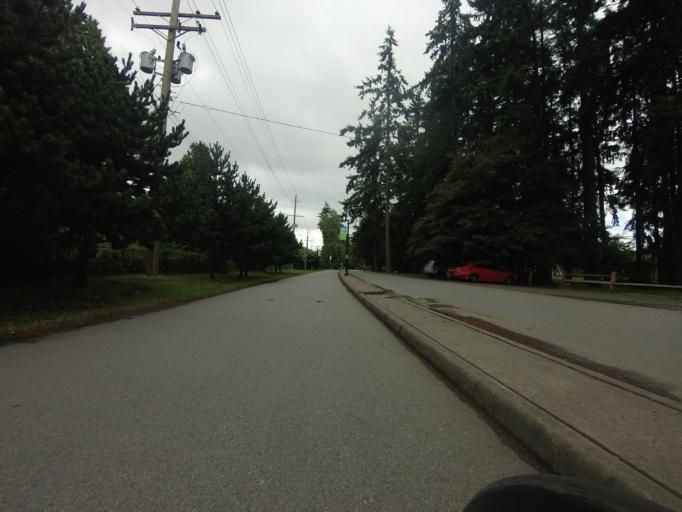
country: CA
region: British Columbia
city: West End
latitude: 49.3250
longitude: -123.1477
